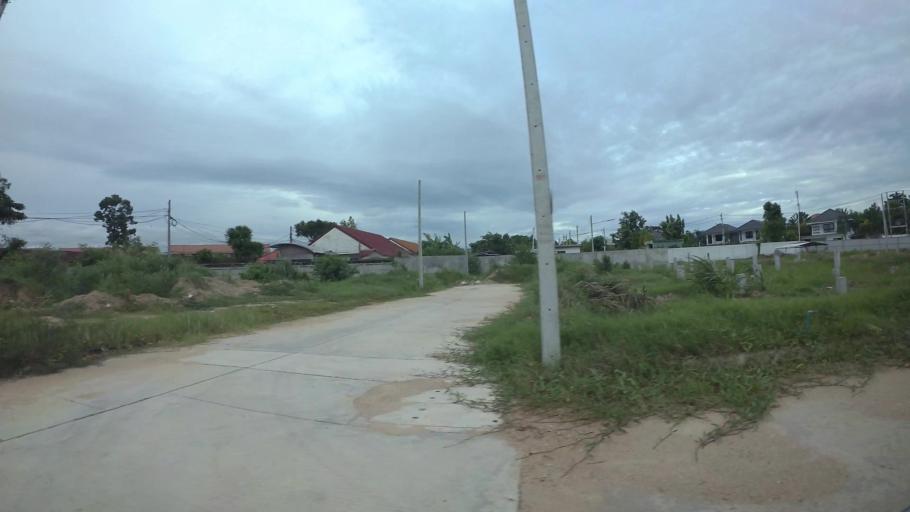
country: TH
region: Chon Buri
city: Si Racha
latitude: 13.1364
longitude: 100.9638
